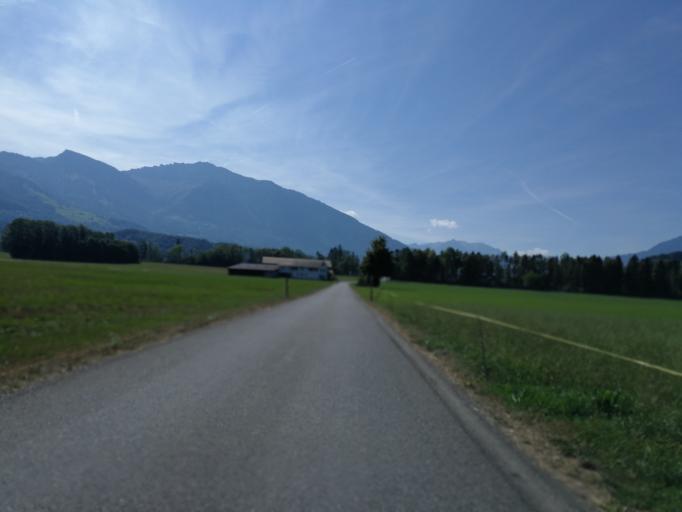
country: CH
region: Saint Gallen
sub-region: Wahlkreis See-Gaster
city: Kaltbrunn
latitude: 47.2073
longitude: 9.0214
